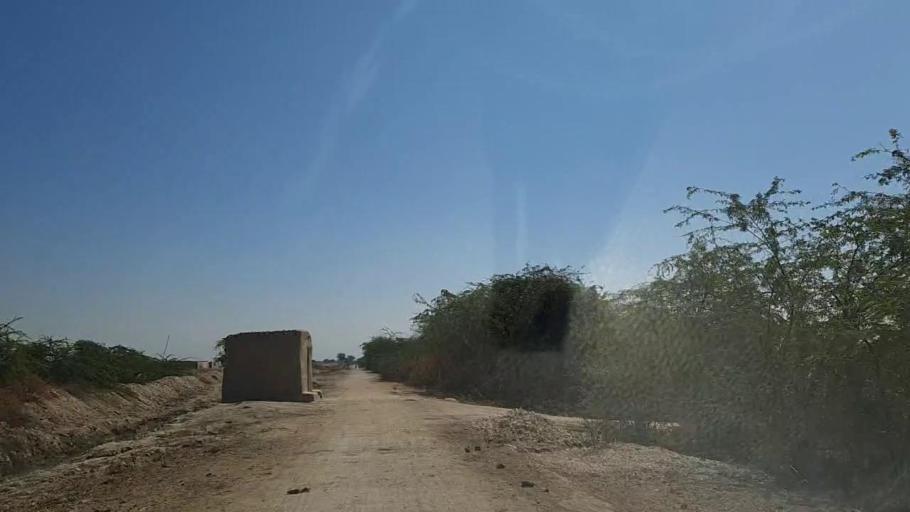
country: PK
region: Sindh
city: Samaro
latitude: 25.3454
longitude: 69.4854
